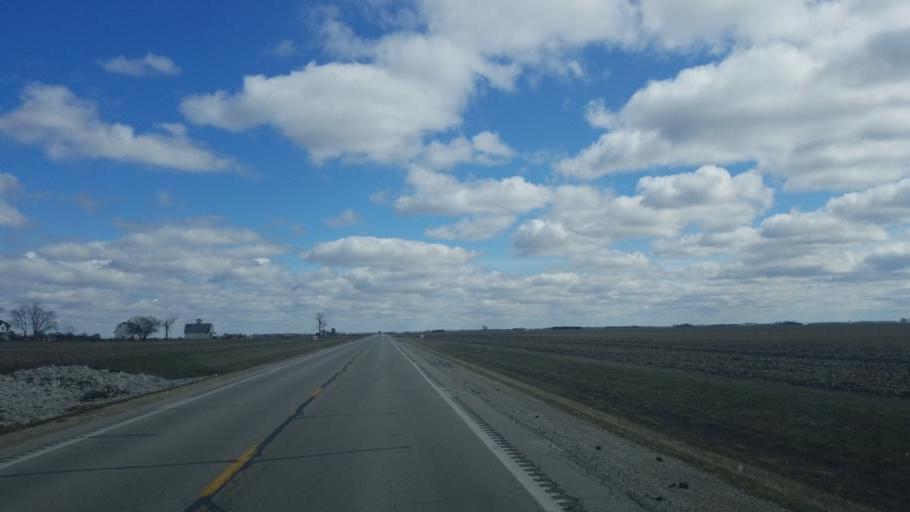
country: US
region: Illinois
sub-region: Douglas County
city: Villa Grove
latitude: 39.7918
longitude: -88.1496
